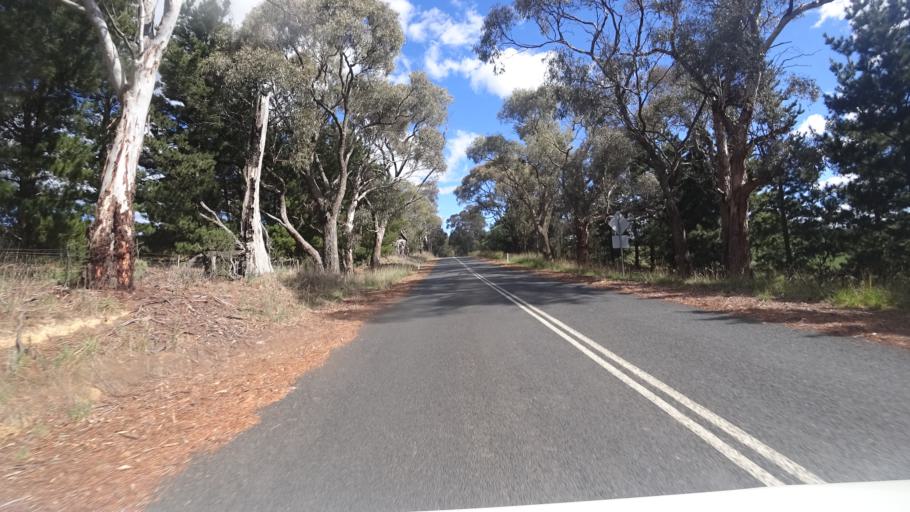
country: AU
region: New South Wales
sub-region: Oberon
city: Oberon
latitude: -33.6810
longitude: 149.7865
